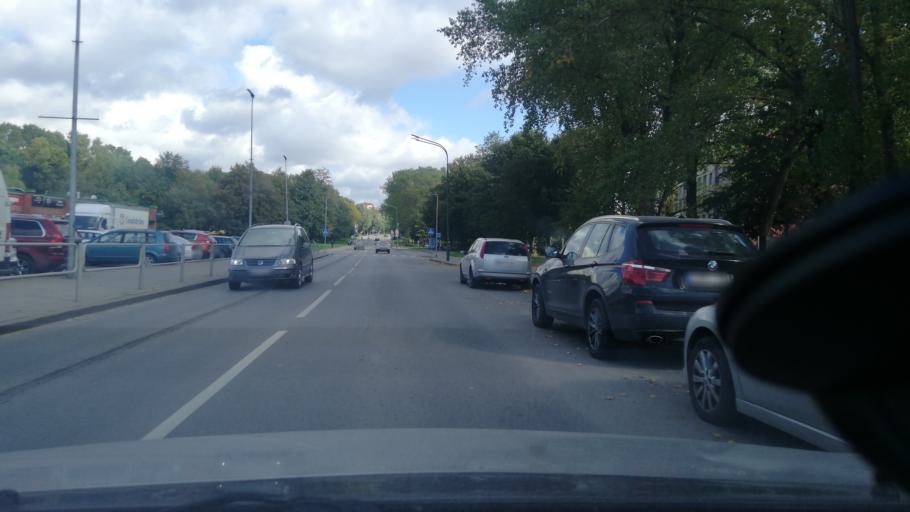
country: LT
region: Klaipedos apskritis
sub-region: Klaipeda
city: Klaipeda
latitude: 55.6822
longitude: 21.1718
